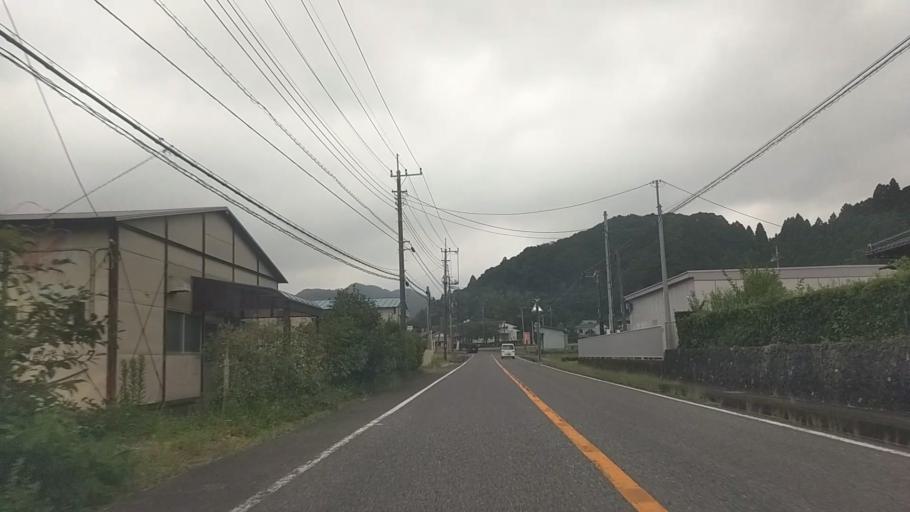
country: JP
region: Chiba
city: Kawaguchi
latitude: 35.1433
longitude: 139.9713
